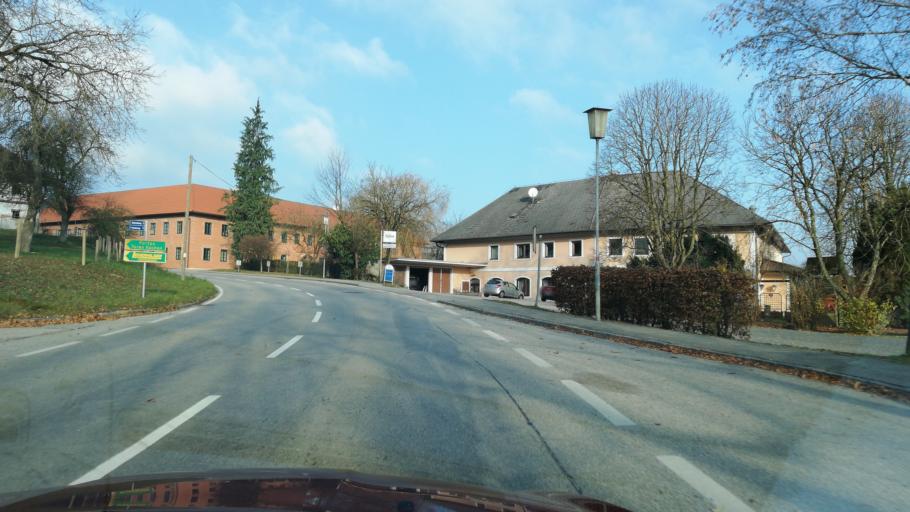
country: AT
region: Upper Austria
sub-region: Wels-Land
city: Marchtrenk
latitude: 48.1254
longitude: 14.0926
